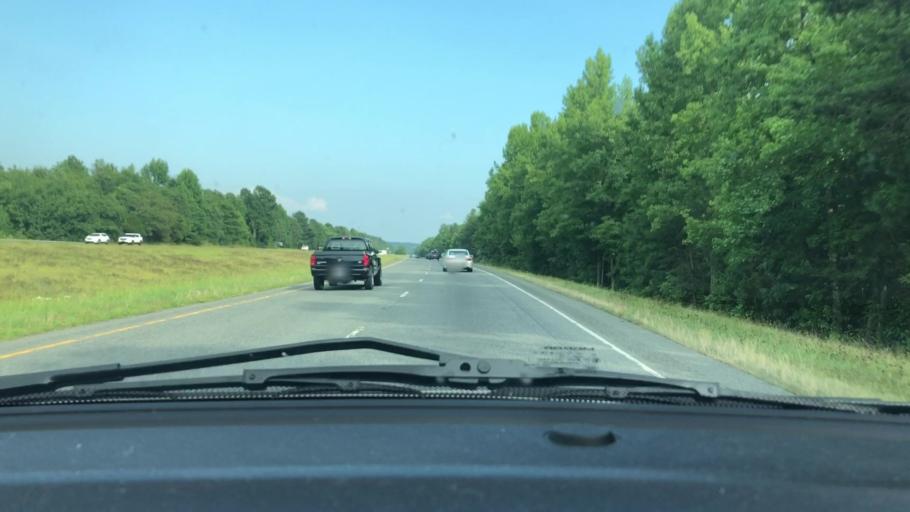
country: US
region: North Carolina
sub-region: Guilford County
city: Forest Oaks
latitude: 35.9010
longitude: -79.6668
